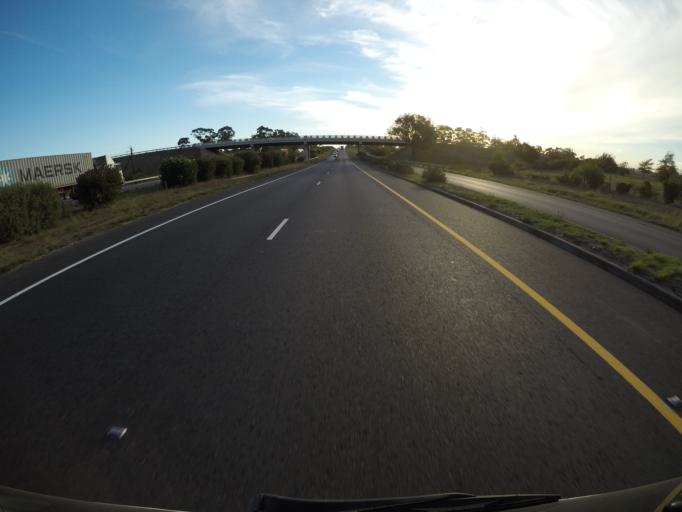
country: ZA
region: Western Cape
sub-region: City of Cape Town
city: Kraaifontein
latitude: -33.8193
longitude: 18.7932
